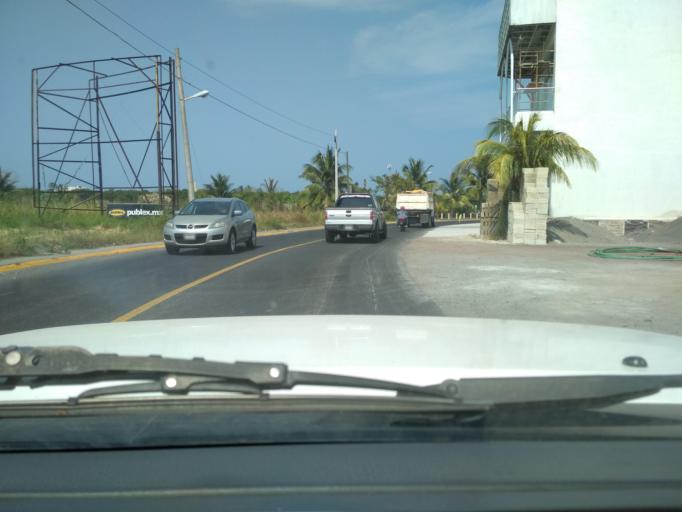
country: MX
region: Veracruz
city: Boca del Rio
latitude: 19.0989
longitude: -96.1145
